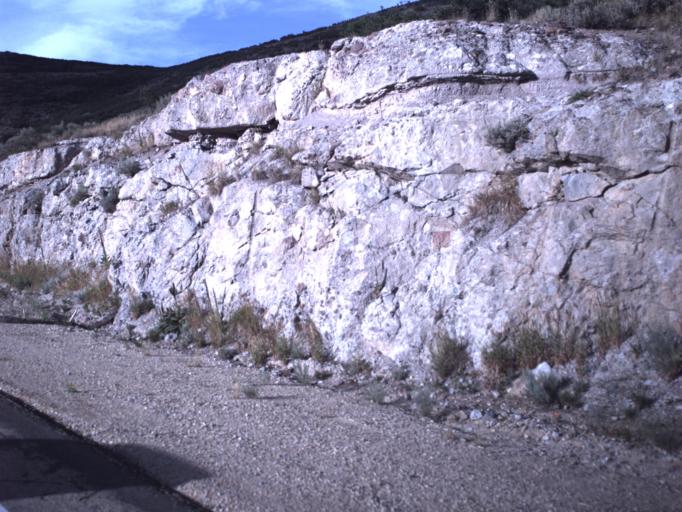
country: US
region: Utah
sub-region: Wasatch County
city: Heber
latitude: 40.5826
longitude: -111.4206
